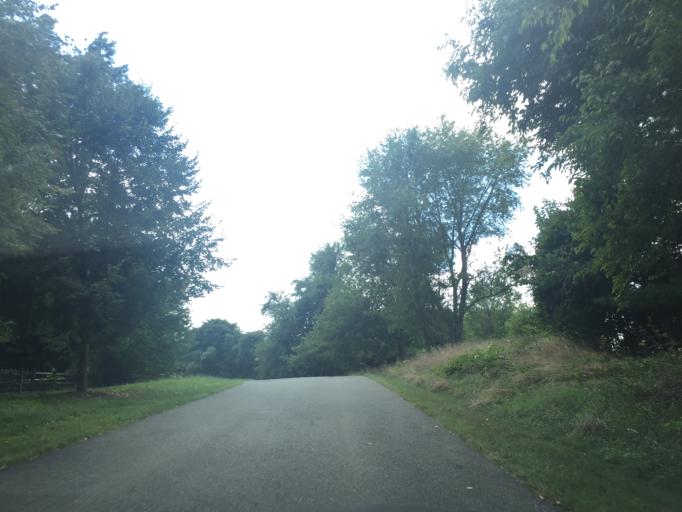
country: US
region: Maryland
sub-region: Montgomery County
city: Montgomery Village
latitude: 39.1644
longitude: -77.1772
